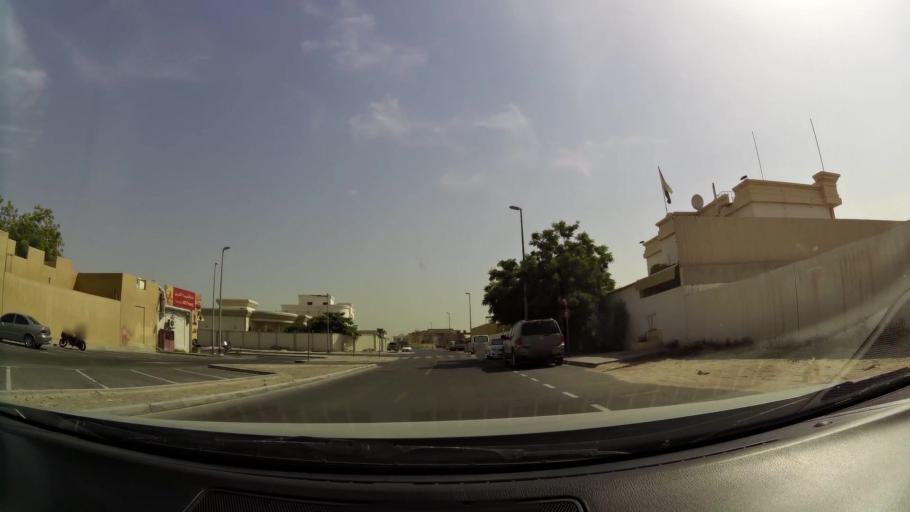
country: AE
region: Ash Shariqah
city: Sharjah
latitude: 25.1996
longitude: 55.4044
